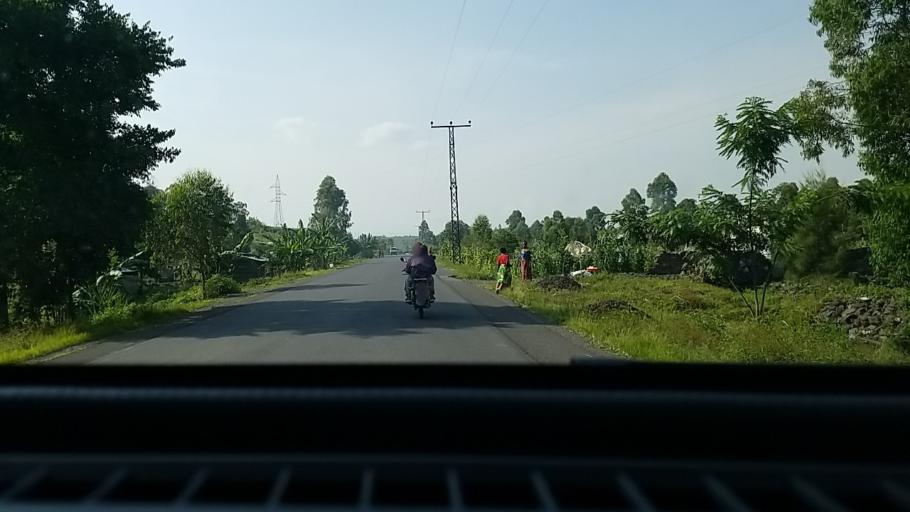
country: CD
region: Nord Kivu
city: Sake
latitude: -1.6125
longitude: 29.1413
